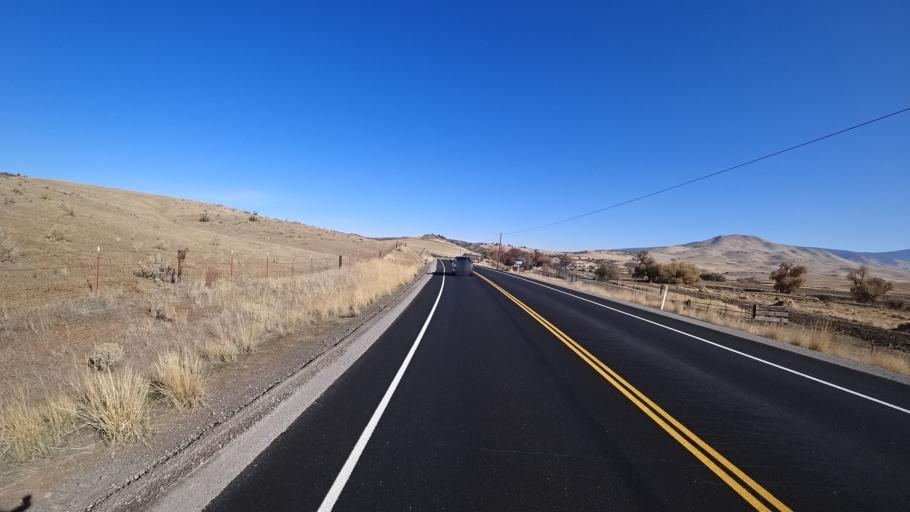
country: US
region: California
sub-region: Siskiyou County
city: Montague
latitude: 41.8428
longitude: -122.4761
